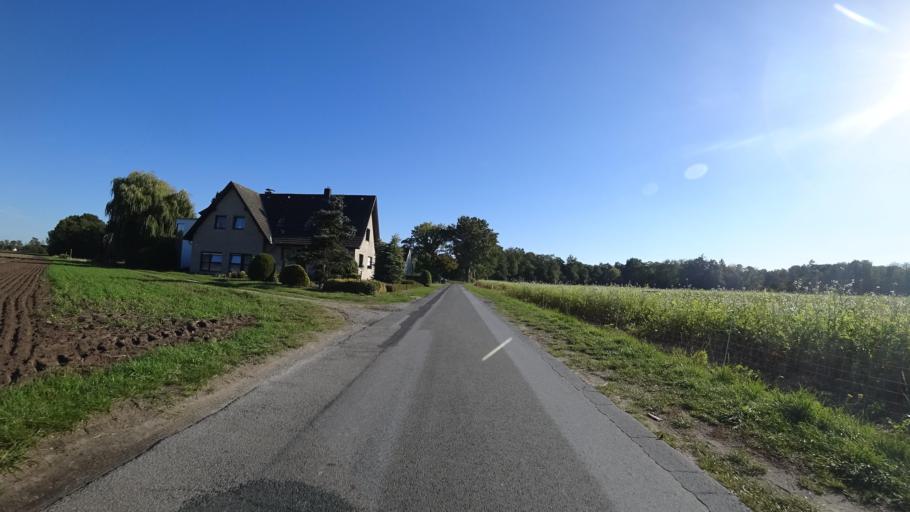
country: DE
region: North Rhine-Westphalia
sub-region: Regierungsbezirk Detmold
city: Guetersloh
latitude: 51.8810
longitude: 8.3573
